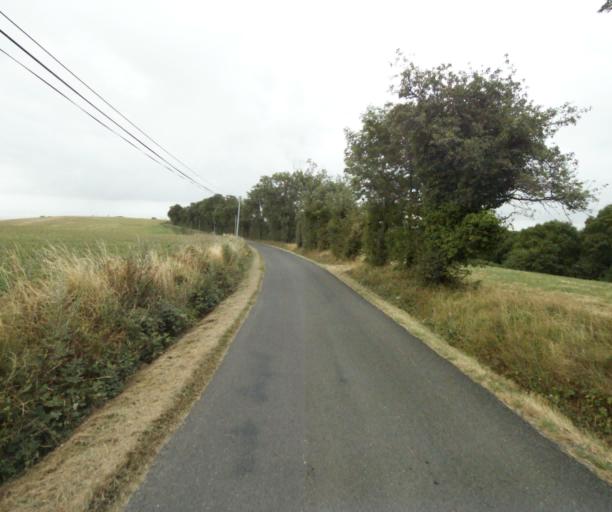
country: FR
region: Midi-Pyrenees
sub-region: Departement du Tarn
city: Soreze
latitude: 43.4004
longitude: 2.0591
